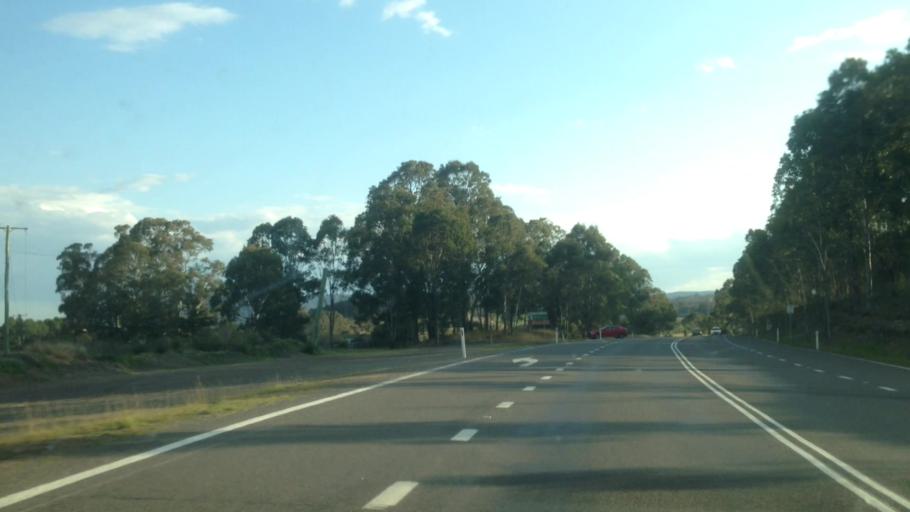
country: AU
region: New South Wales
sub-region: Cessnock
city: Kurri Kurri
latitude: -32.8716
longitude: 151.4783
